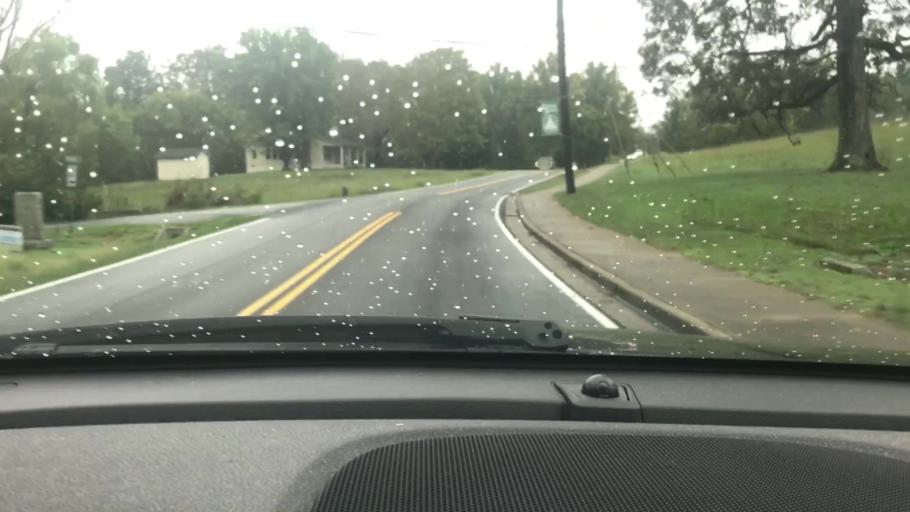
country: US
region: Tennessee
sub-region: Cheatham County
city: Kingston Springs
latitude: 36.0979
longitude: -87.1130
